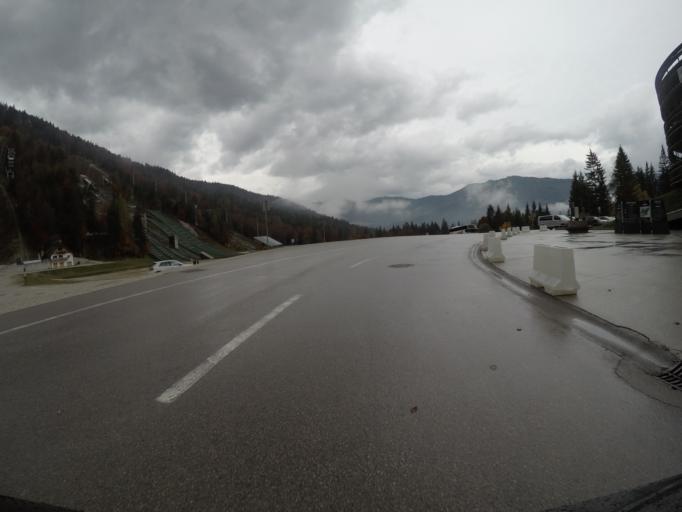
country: SI
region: Kranjska Gora
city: Kranjska Gora
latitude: 46.4760
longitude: 13.7240
